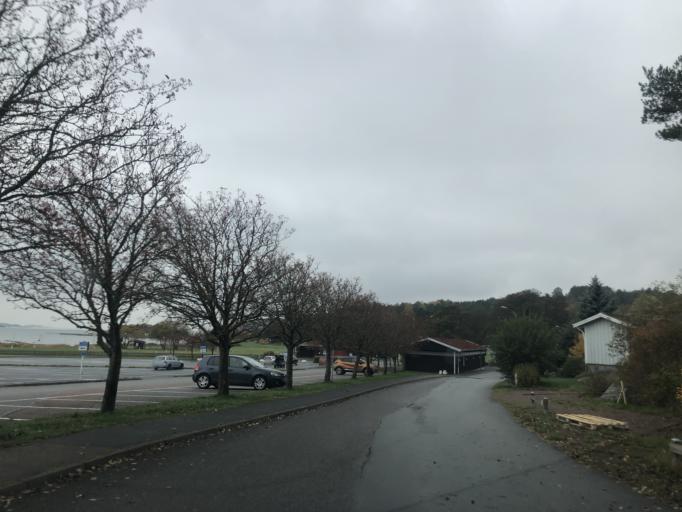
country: SE
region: Vaestra Goetaland
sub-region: Goteborg
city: Majorna
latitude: 57.6294
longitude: 11.9227
